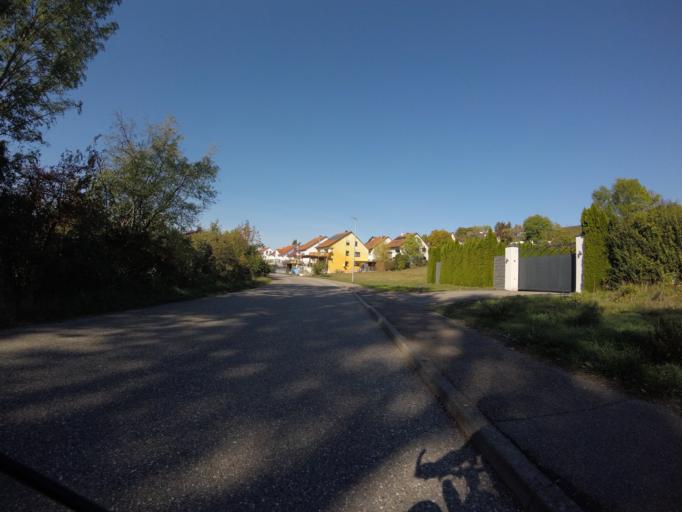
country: DE
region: Baden-Wuerttemberg
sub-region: Regierungsbezirk Stuttgart
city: Sersheim
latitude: 48.9845
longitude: 8.9834
